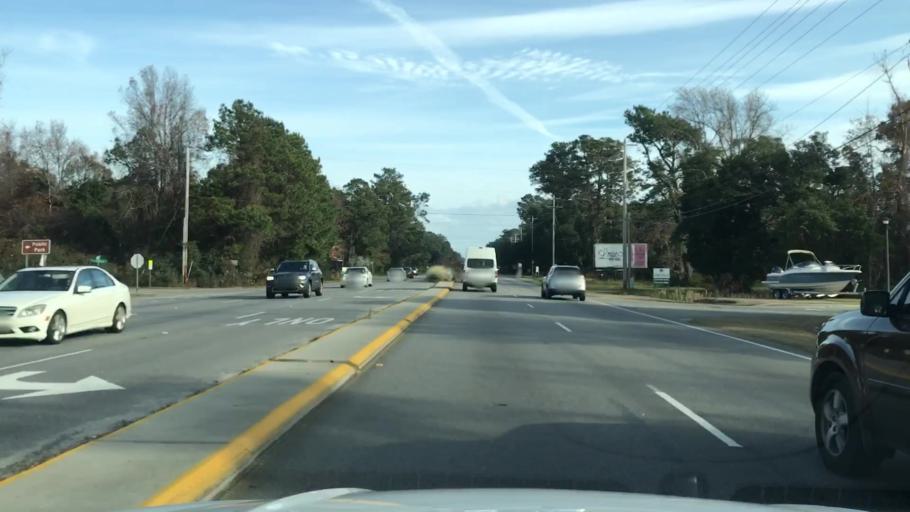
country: US
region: South Carolina
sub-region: Georgetown County
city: Murrells Inlet
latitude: 33.4507
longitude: -79.1188
